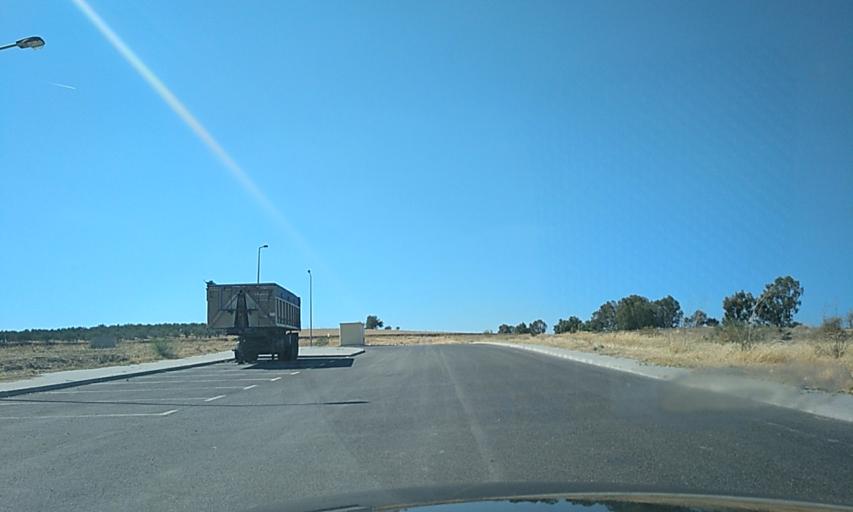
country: PT
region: Portalegre
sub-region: Campo Maior
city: Campo Maior
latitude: 39.0258
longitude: -7.0603
